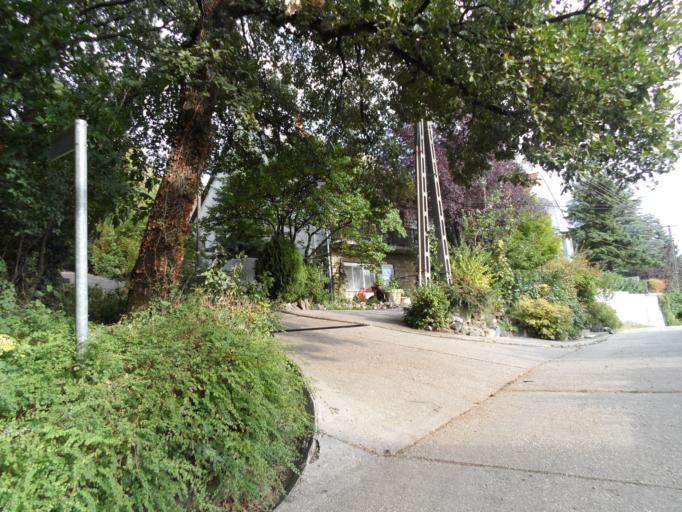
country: HU
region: Somogy
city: Fonyod
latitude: 46.7439
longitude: 17.5492
